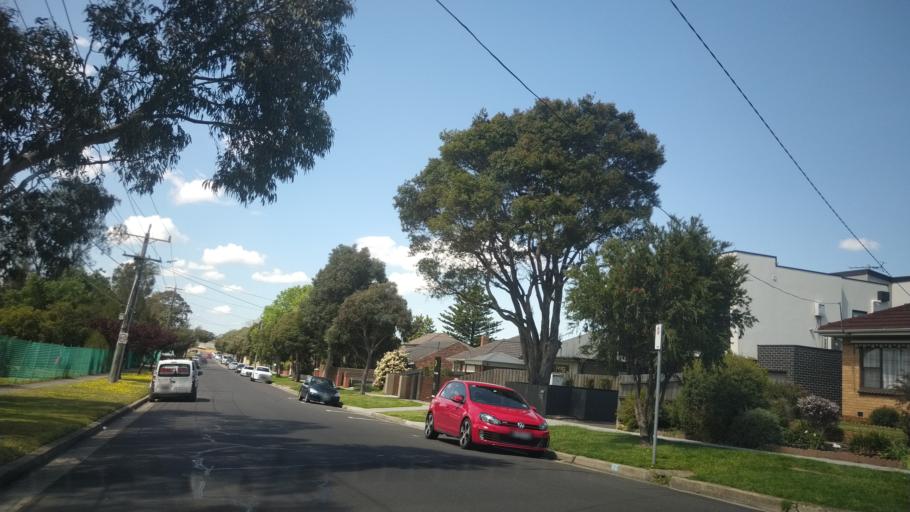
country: AU
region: Victoria
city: Highett
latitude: -37.9516
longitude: 145.0530
